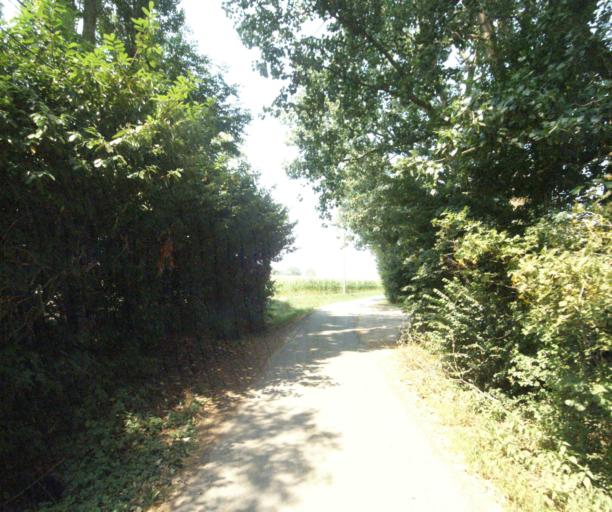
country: FR
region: Nord-Pas-de-Calais
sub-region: Departement du Nord
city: Wambrechies
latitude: 50.7086
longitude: 3.0440
